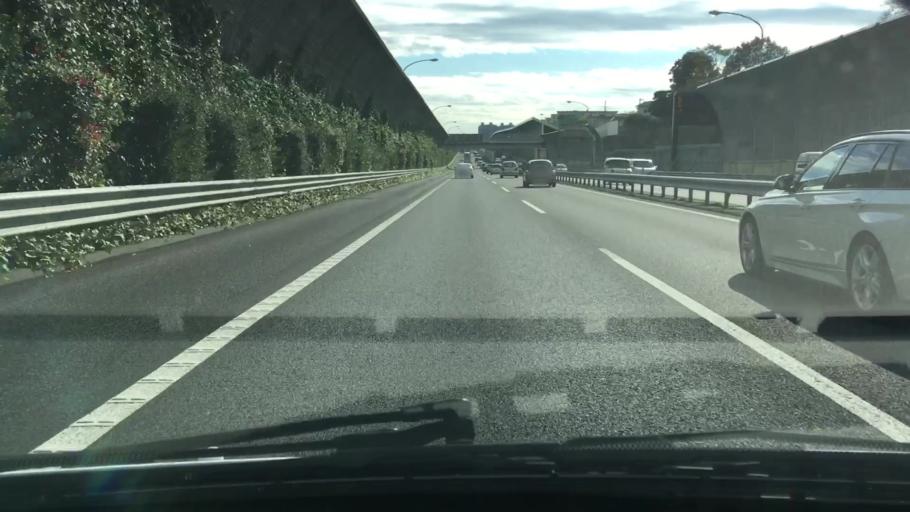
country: JP
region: Chiba
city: Chiba
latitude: 35.6402
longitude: 140.1162
